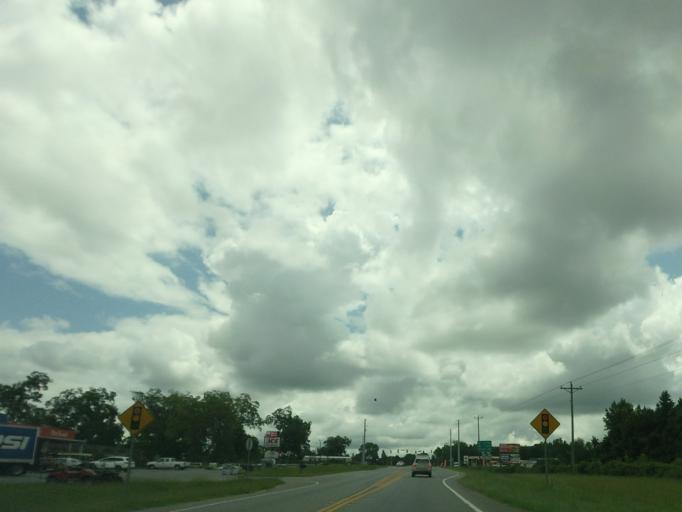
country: US
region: Georgia
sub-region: Bleckley County
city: Cochran
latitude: 32.4034
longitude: -83.3374
